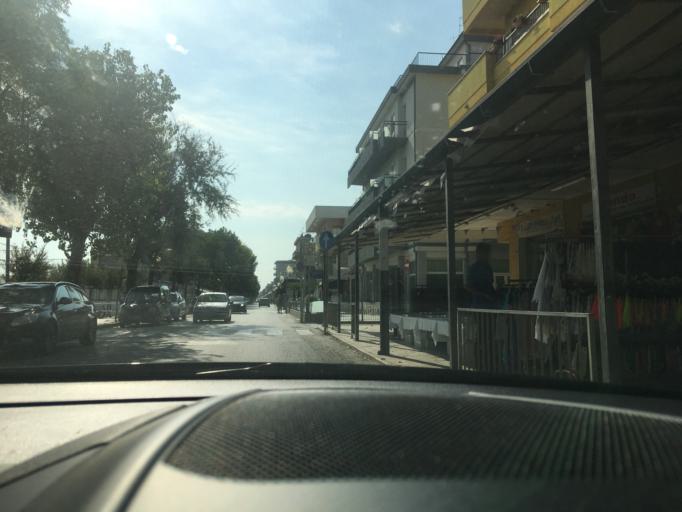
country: IT
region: Emilia-Romagna
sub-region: Provincia di Rimini
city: Santa Giustina
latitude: 44.1093
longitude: 12.5099
